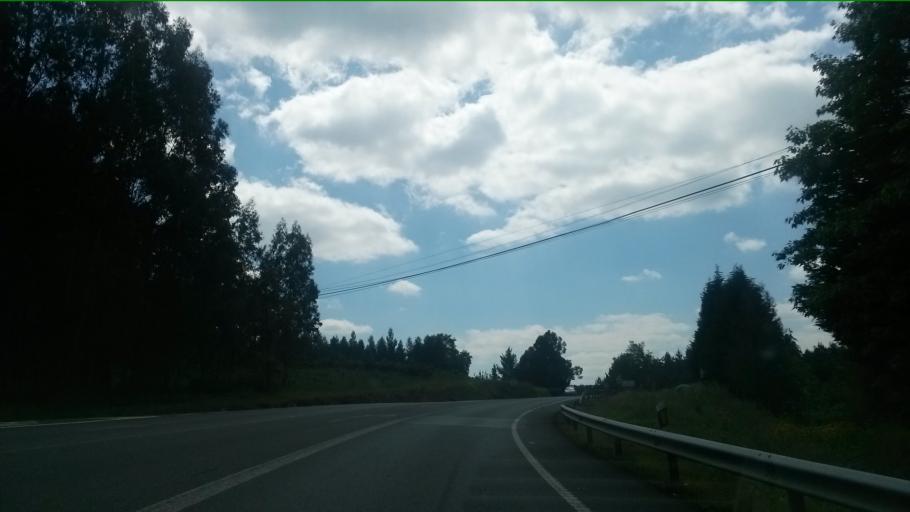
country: ES
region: Galicia
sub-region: Provincia da Coruna
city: Touro
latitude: 42.9473
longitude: -8.3377
